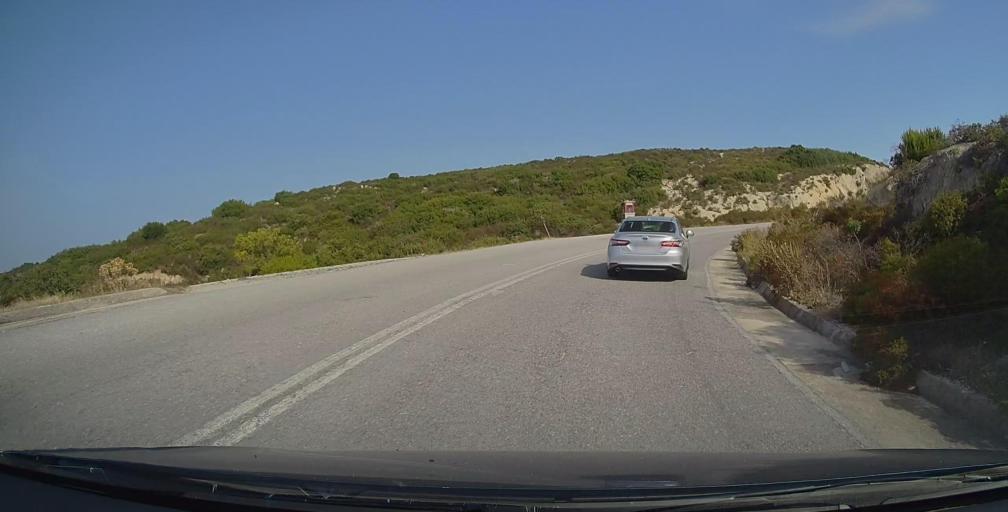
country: GR
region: Central Macedonia
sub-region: Nomos Chalkidikis
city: Sykia
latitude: 39.9796
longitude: 23.9587
